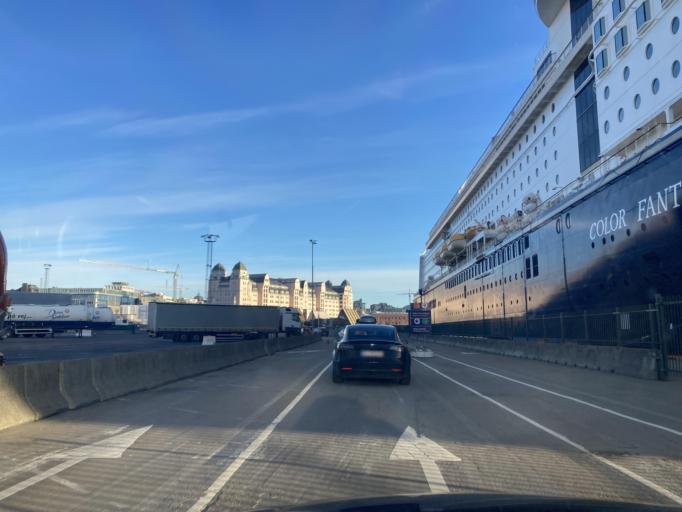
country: NO
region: Oslo
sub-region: Oslo
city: Oslo
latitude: 59.9042
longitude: 10.7452
